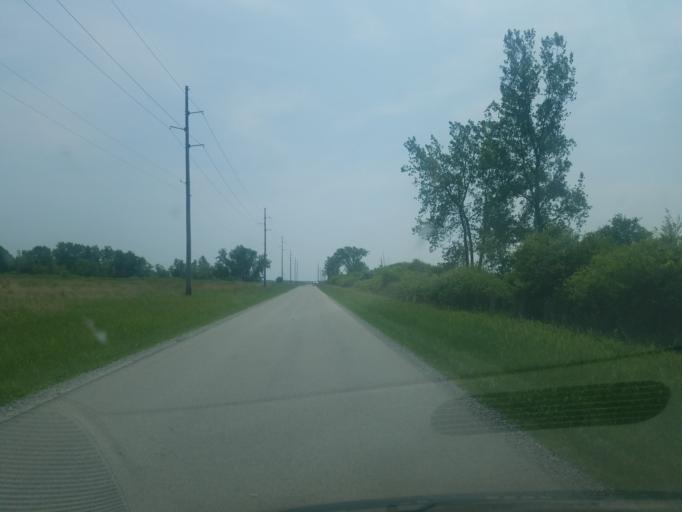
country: US
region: Ohio
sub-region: Wyandot County
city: Upper Sandusky
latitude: 40.7061
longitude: -83.2991
